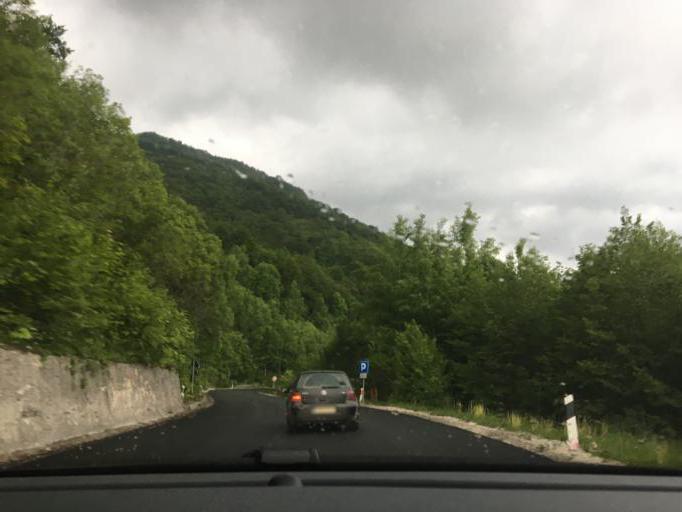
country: MK
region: Gostivar
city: Vrutok
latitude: 41.6745
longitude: 20.8499
